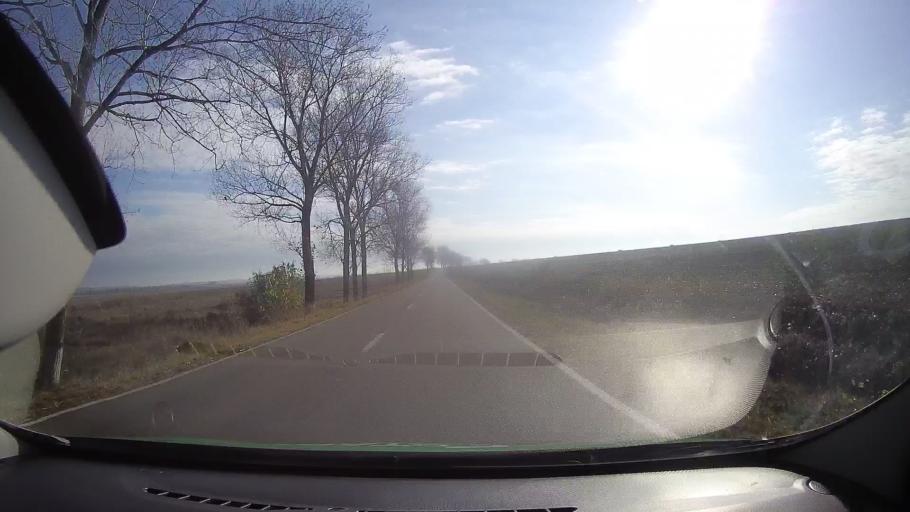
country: RO
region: Tulcea
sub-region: Comuna Mahmudia
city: Mahmudia
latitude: 45.0684
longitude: 29.1020
